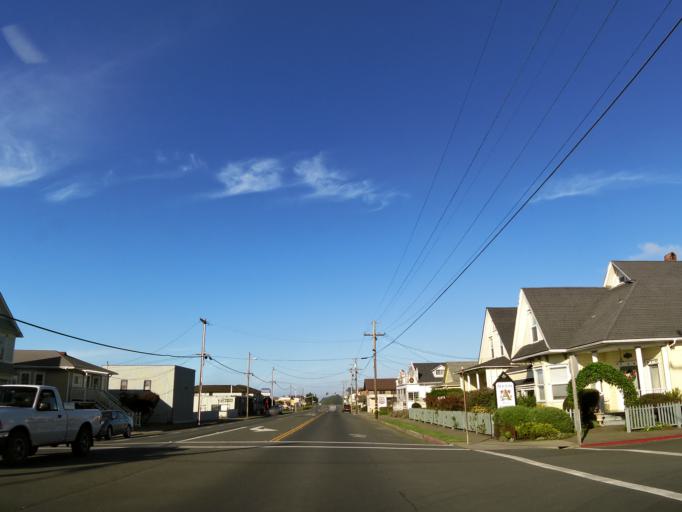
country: US
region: California
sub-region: Mendocino County
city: Fort Bragg
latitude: 39.4491
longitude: -123.8059
